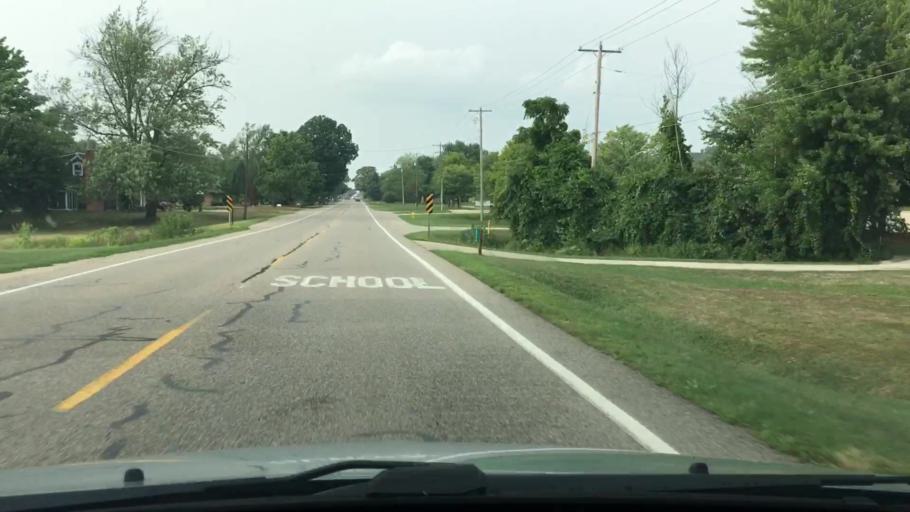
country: US
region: Michigan
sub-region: Ottawa County
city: Hudsonville
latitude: 42.9149
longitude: -85.9024
